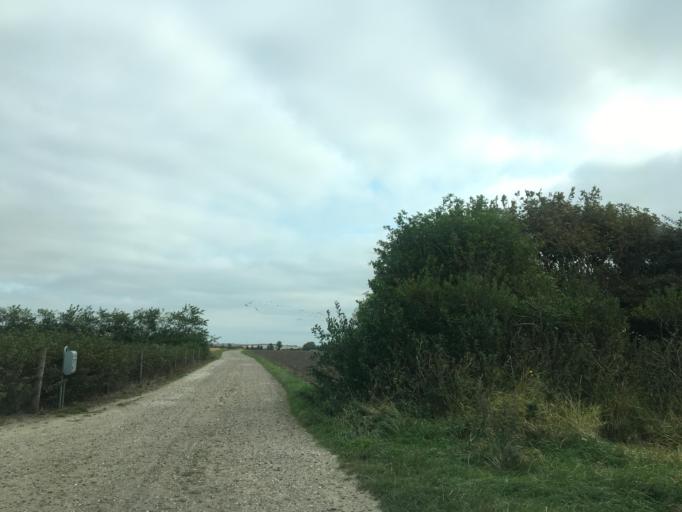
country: DK
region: Central Jutland
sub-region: Lemvig Kommune
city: Thyboron
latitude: 56.7884
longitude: 8.2793
